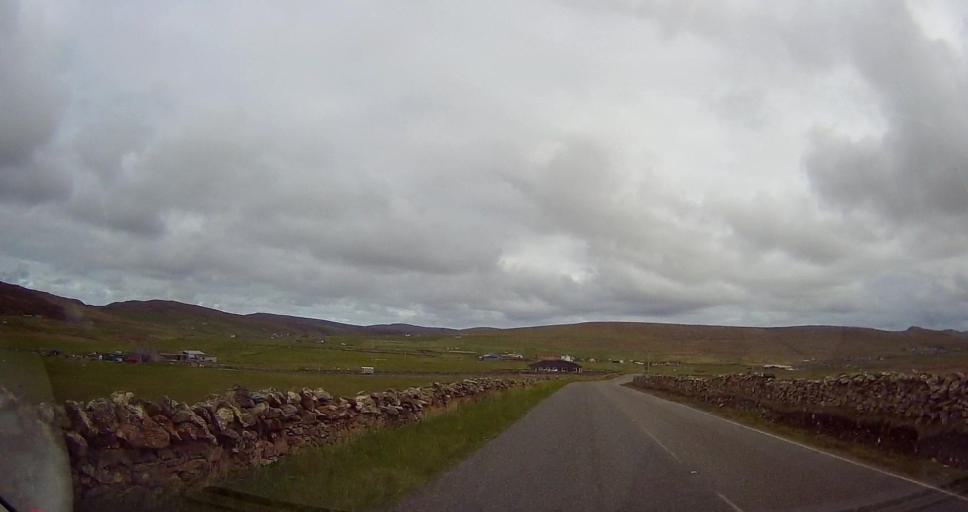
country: GB
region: Scotland
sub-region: Shetland Islands
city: Shetland
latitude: 60.7511
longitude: -0.8856
